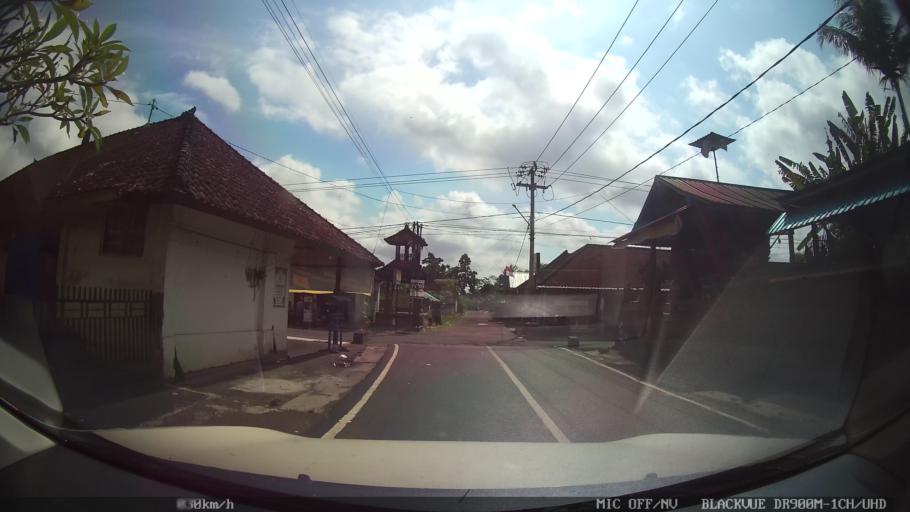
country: ID
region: Bali
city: Banjar Pesalakan
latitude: -8.5193
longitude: 115.3031
